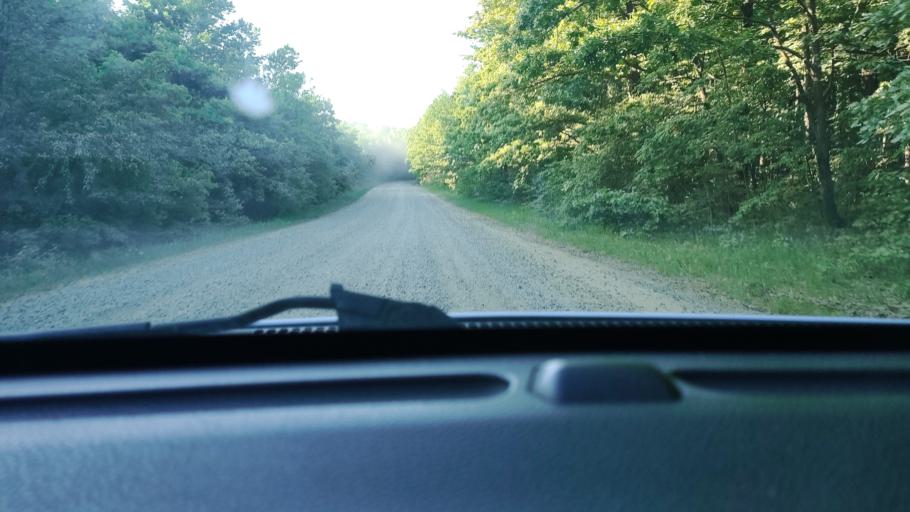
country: RU
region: Krasnodarskiy
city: Goryachiy Klyuch
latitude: 44.7113
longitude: 38.9919
